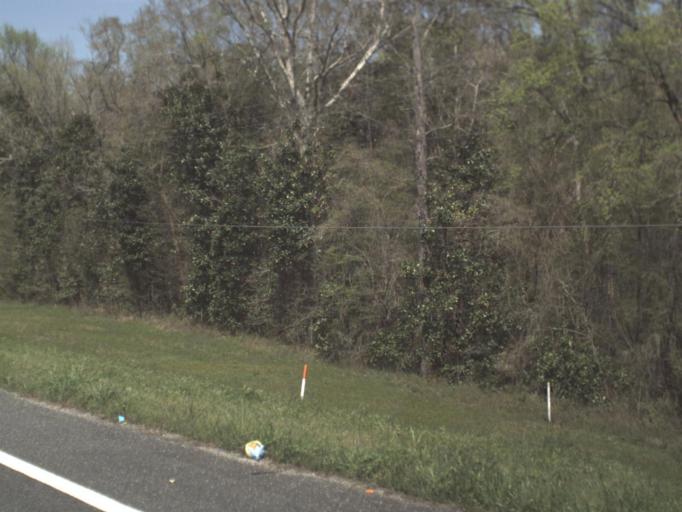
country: US
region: Florida
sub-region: Gadsden County
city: Midway
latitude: 30.5288
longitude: -84.4720
